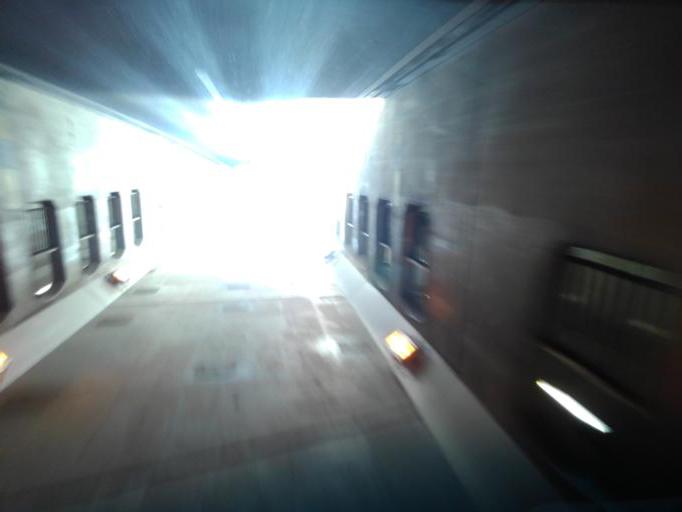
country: JP
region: Saitama
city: Tokorozawa
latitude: 35.8042
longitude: 139.4588
